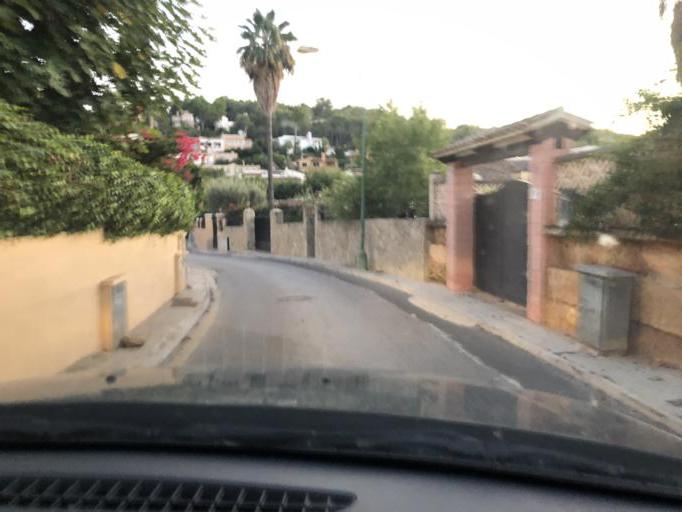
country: ES
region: Balearic Islands
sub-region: Illes Balears
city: Santa Ponsa
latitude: 39.5255
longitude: 2.4825
